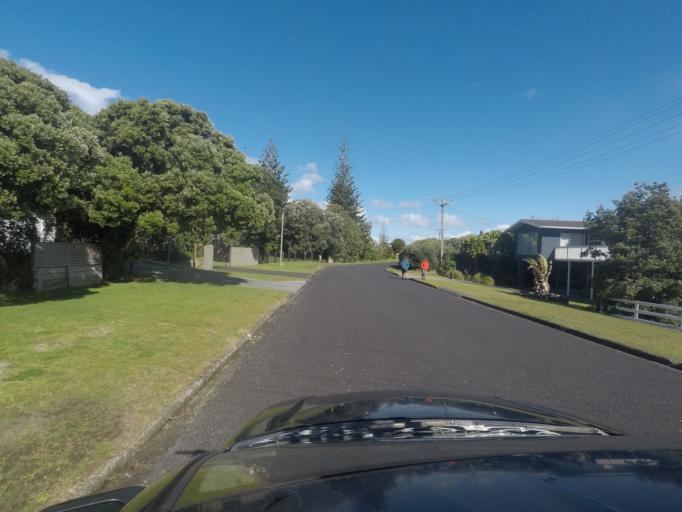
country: NZ
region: Bay of Plenty
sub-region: Western Bay of Plenty District
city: Waihi Beach
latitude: -37.4176
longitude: 175.9506
